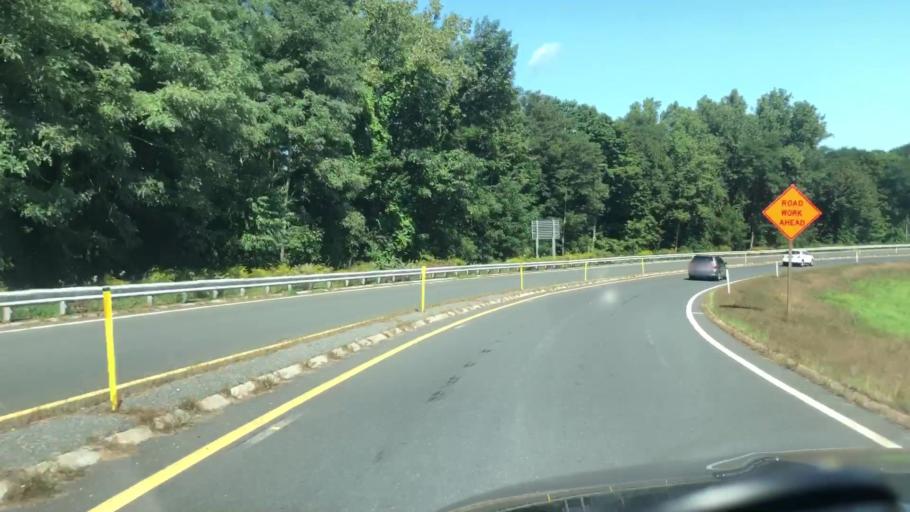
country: US
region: Massachusetts
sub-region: Franklin County
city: Bernardston
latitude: 42.6710
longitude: -72.5449
